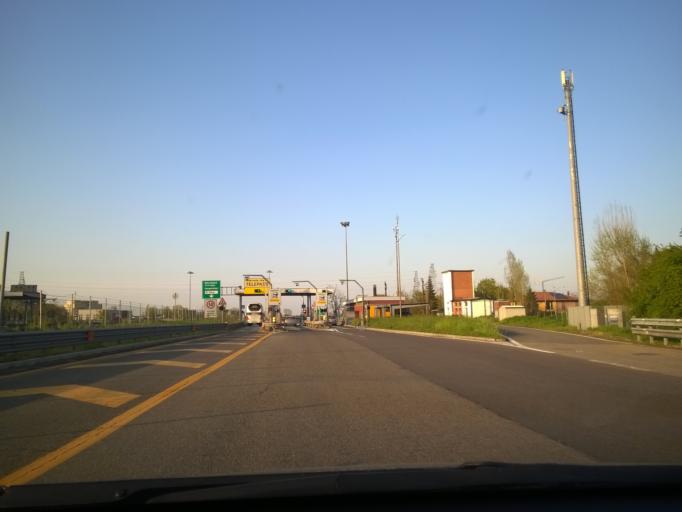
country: IT
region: Emilia-Romagna
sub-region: Provincia di Bologna
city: Progresso
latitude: 44.5301
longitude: 11.3602
